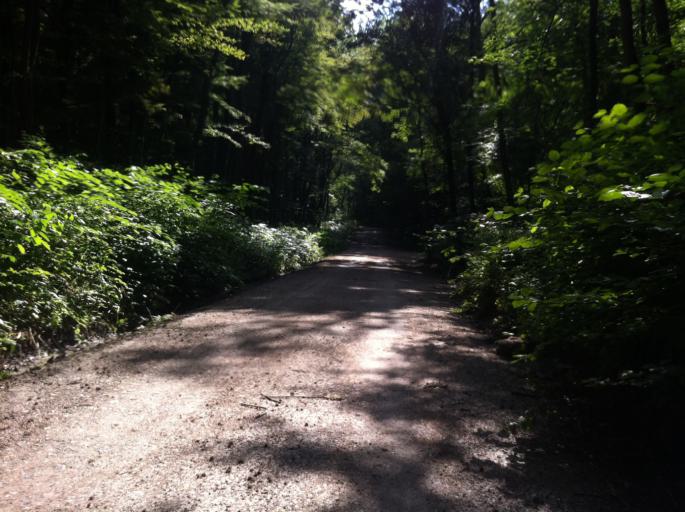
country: AT
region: Lower Austria
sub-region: Politischer Bezirk Modling
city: Laab im Walde
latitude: 48.1805
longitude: 16.1684
